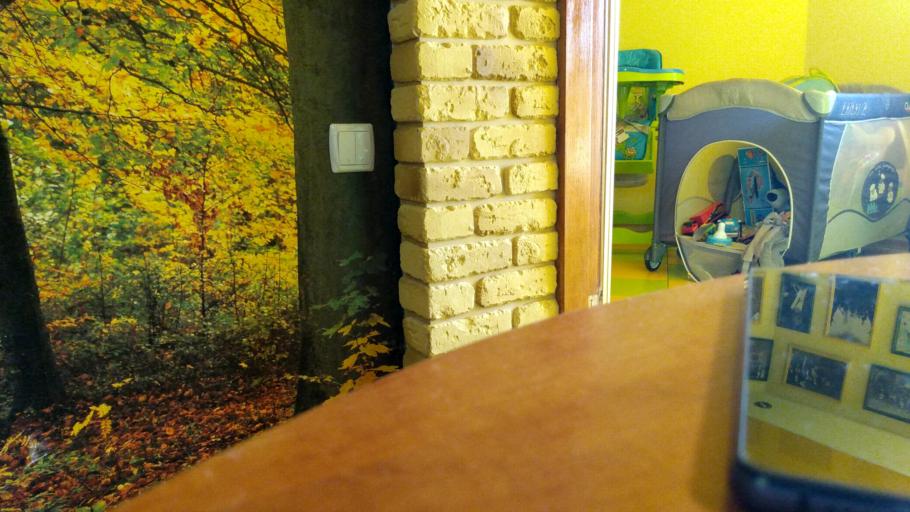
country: RU
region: Tverskaya
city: Likhoslavl'
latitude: 57.2713
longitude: 35.3899
